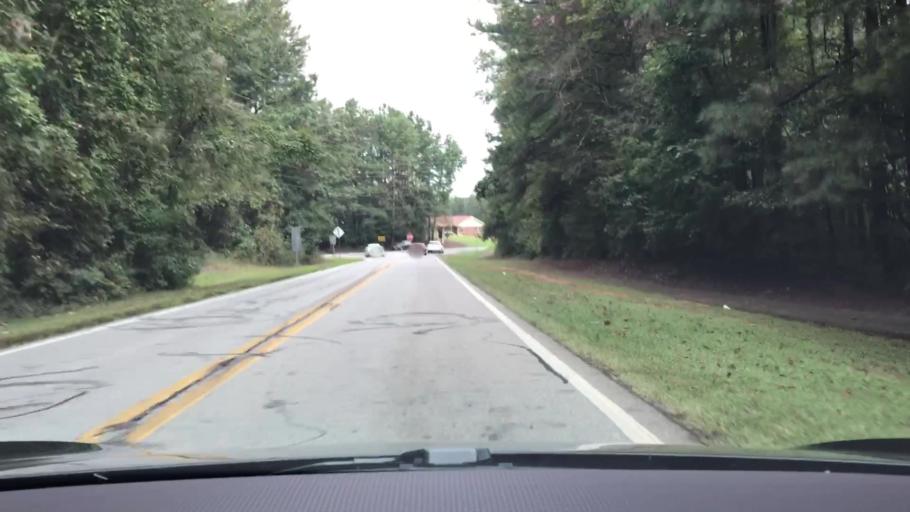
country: US
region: Georgia
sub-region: Barrow County
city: Auburn
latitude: 34.0894
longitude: -83.8697
